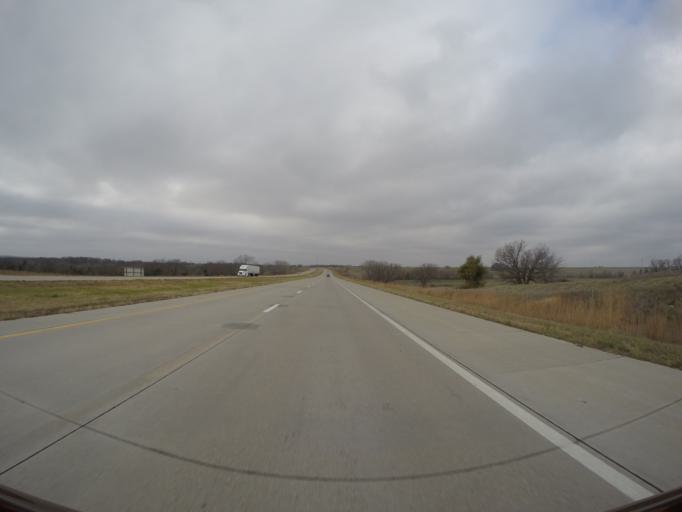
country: US
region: Kansas
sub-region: Geary County
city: Junction City
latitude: 39.0009
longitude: -96.9075
